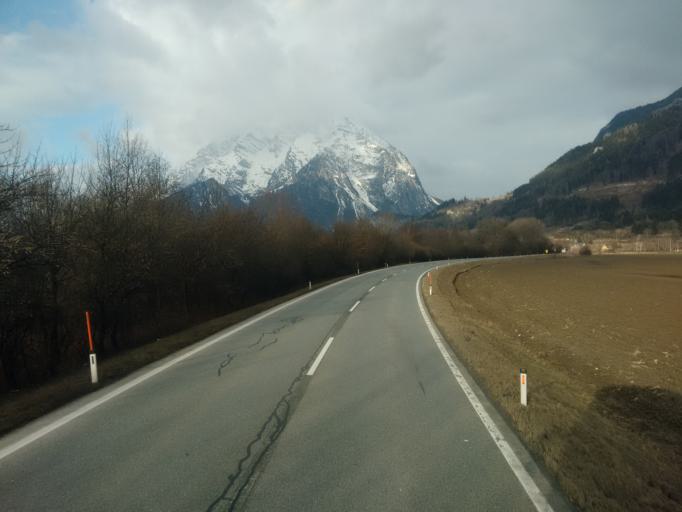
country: AT
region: Styria
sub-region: Politischer Bezirk Liezen
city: Stainach
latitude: 47.5248
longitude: 14.1034
